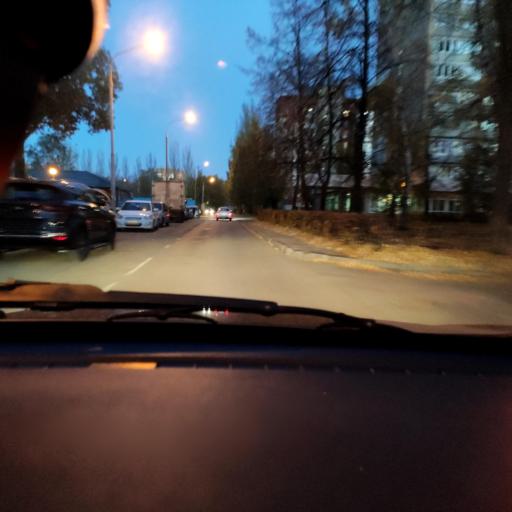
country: RU
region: Samara
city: Tol'yatti
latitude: 53.5327
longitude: 49.2899
